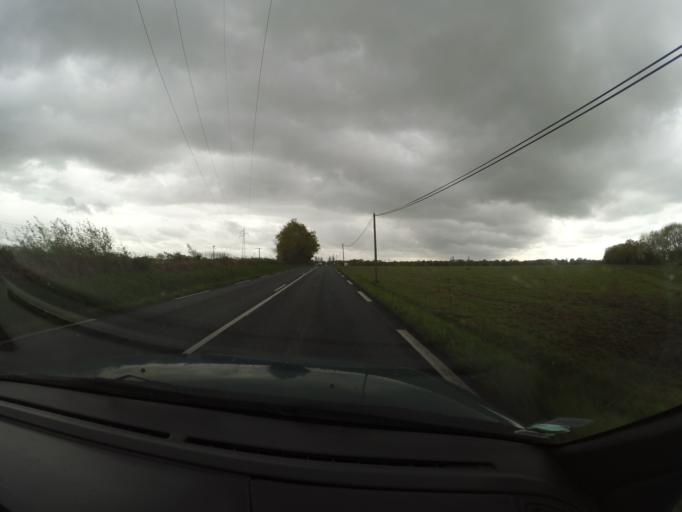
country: FR
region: Pays de la Loire
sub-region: Departement de la Loire-Atlantique
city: Vallet
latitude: 47.1969
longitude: -1.2484
